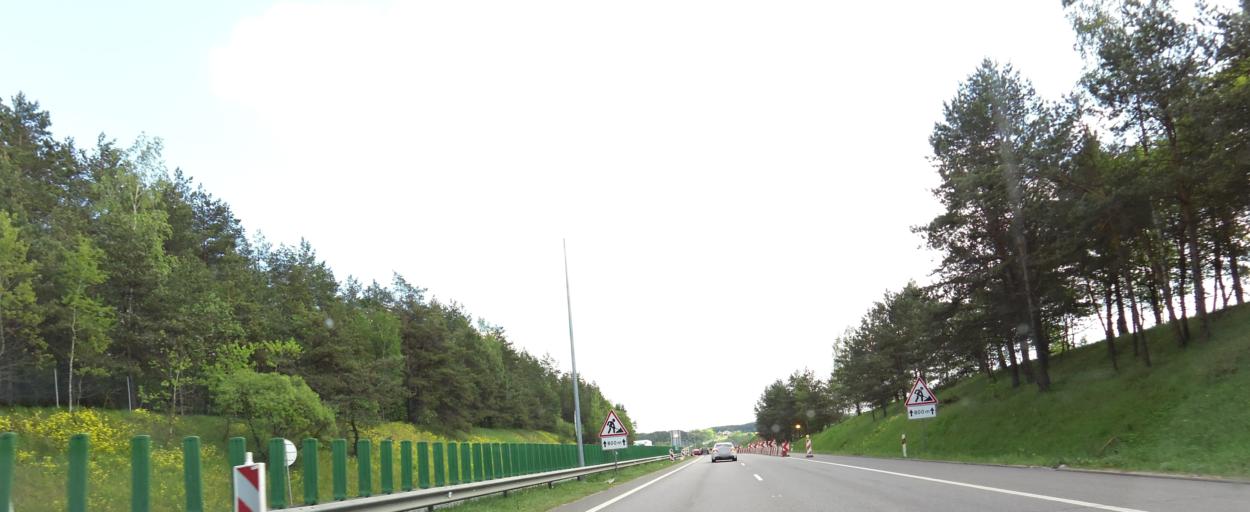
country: LT
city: Lentvaris
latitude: 54.6942
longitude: 25.0275
